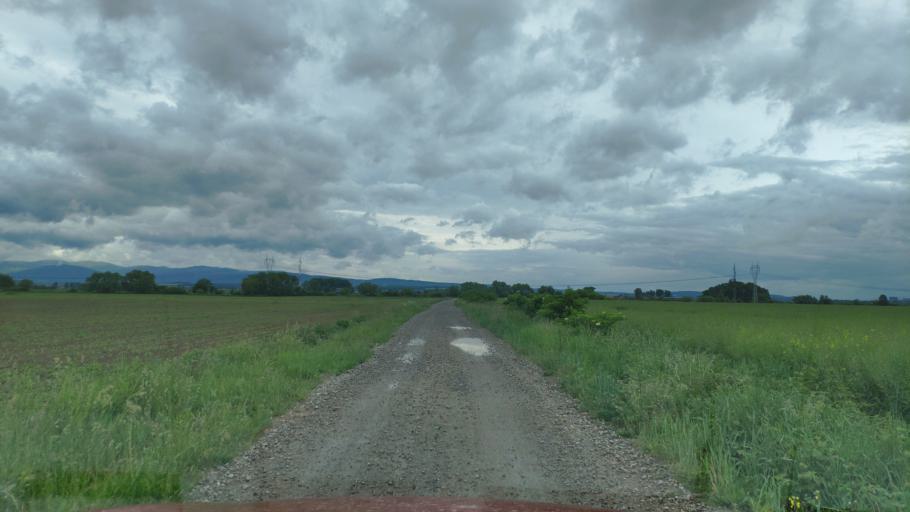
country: SK
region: Kosicky
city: Moldava nad Bodvou
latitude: 48.5572
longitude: 21.1157
